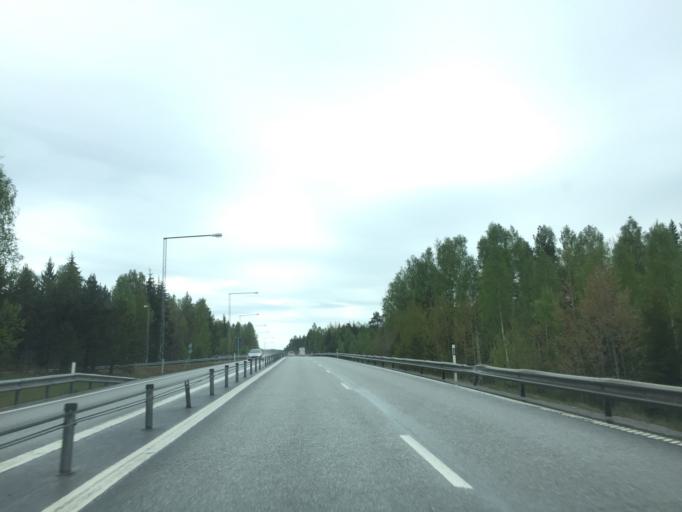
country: SE
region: OErebro
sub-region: Nora Kommun
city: Nora
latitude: 59.4693
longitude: 15.1327
